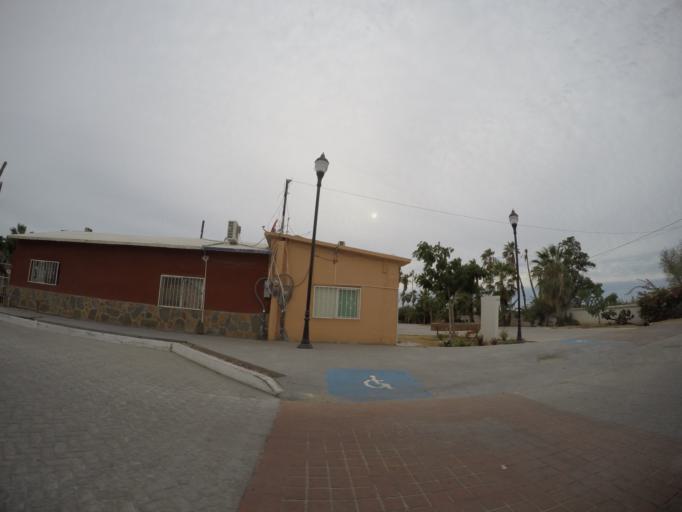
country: MX
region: Baja California Sur
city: Todos Santos
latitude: 23.4469
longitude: -110.2270
